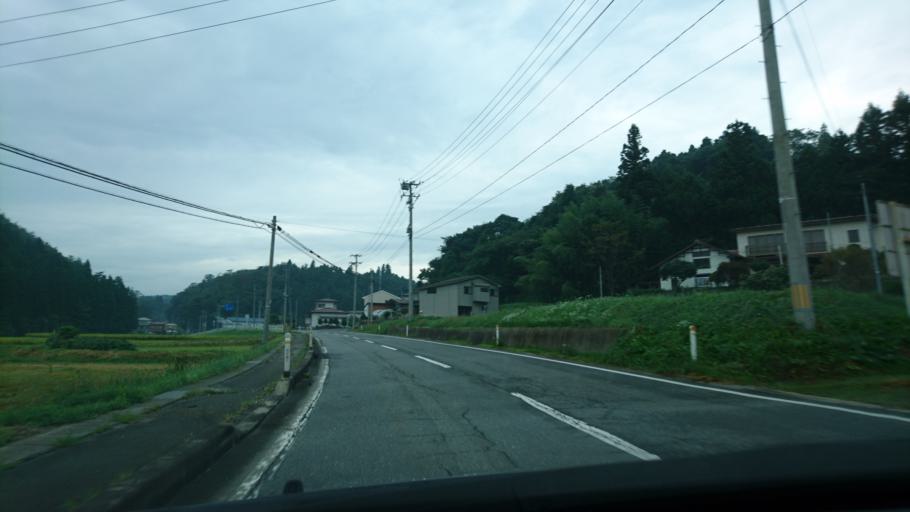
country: JP
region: Iwate
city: Ichinoseki
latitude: 39.0107
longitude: 141.2627
